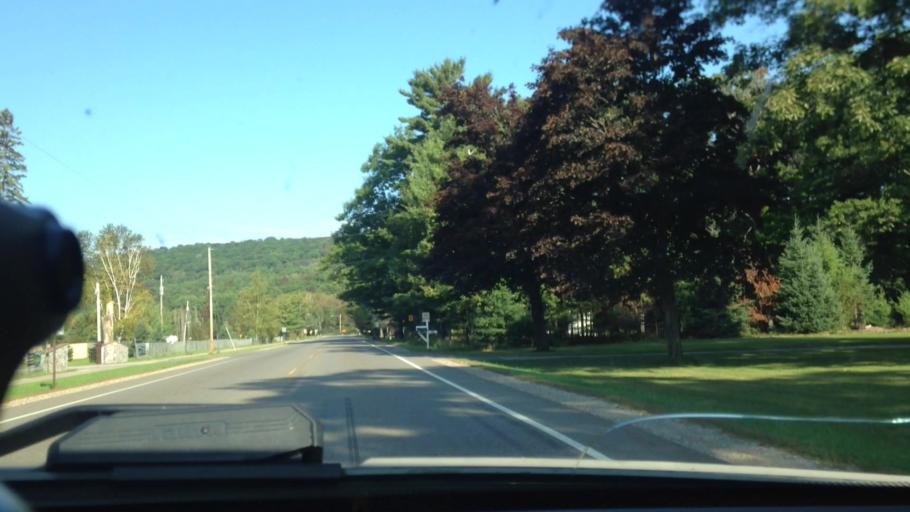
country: US
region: Michigan
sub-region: Dickinson County
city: Quinnesec
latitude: 45.8407
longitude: -88.0148
